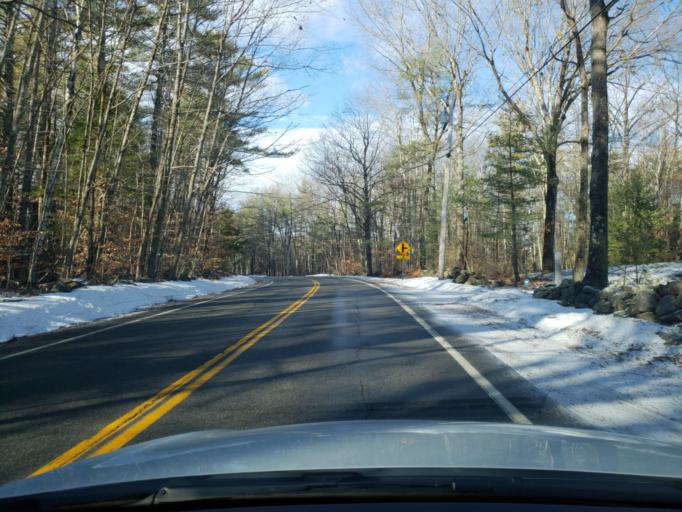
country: US
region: New Hampshire
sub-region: Hillsborough County
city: Lyndeborough
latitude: 42.9845
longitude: -71.7898
